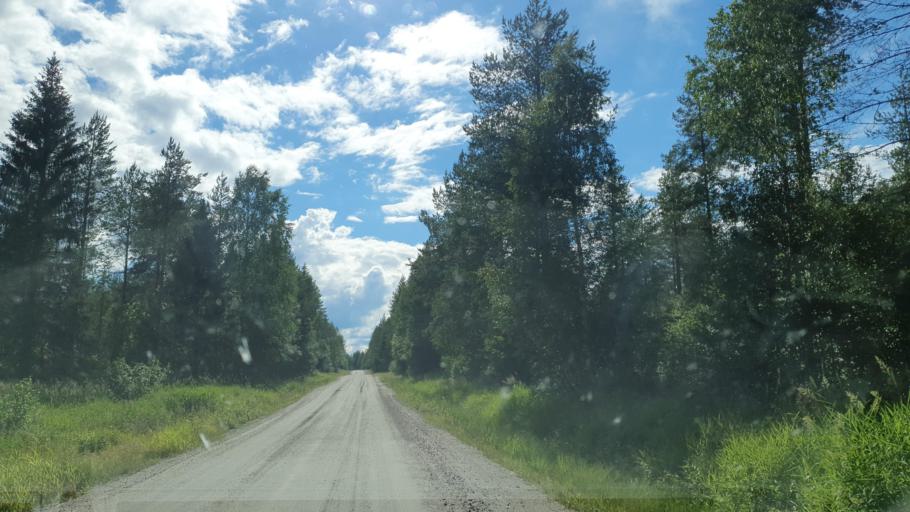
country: FI
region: Kainuu
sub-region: Kehys-Kainuu
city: Kuhmo
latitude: 64.1460
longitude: 29.7125
